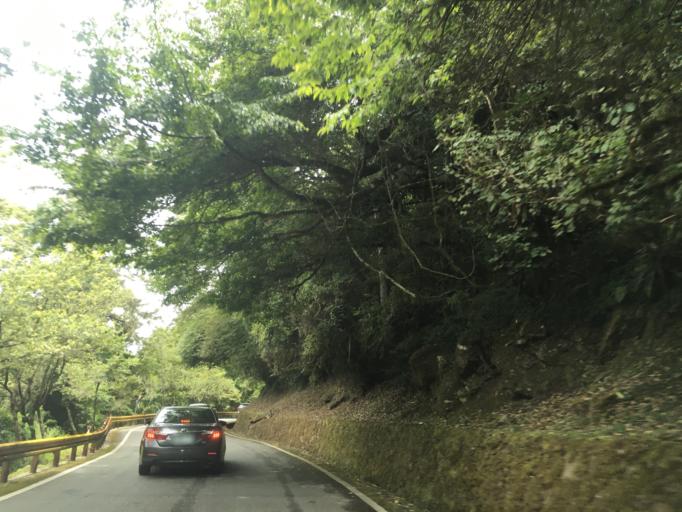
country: TW
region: Taiwan
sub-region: Hualien
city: Hualian
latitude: 24.1786
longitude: 121.3900
